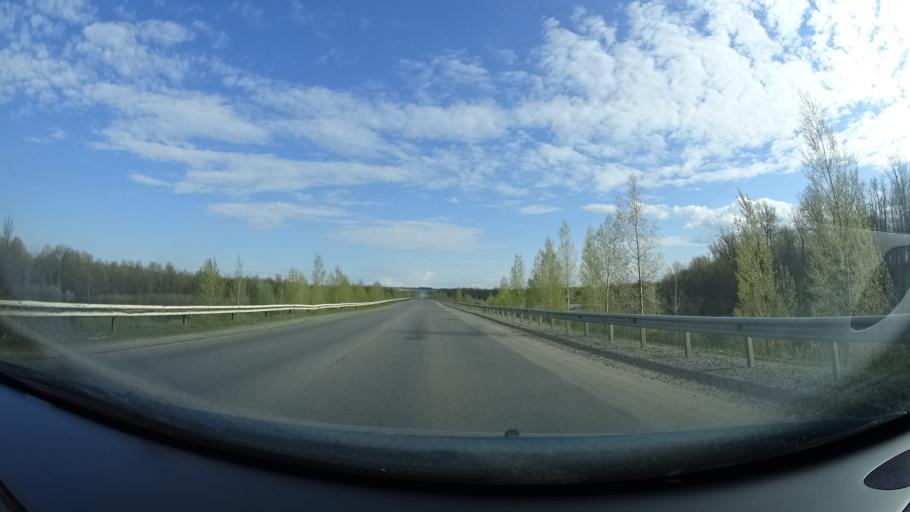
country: RU
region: Bashkortostan
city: Blagoveshchensk
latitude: 55.0478
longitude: 55.8096
